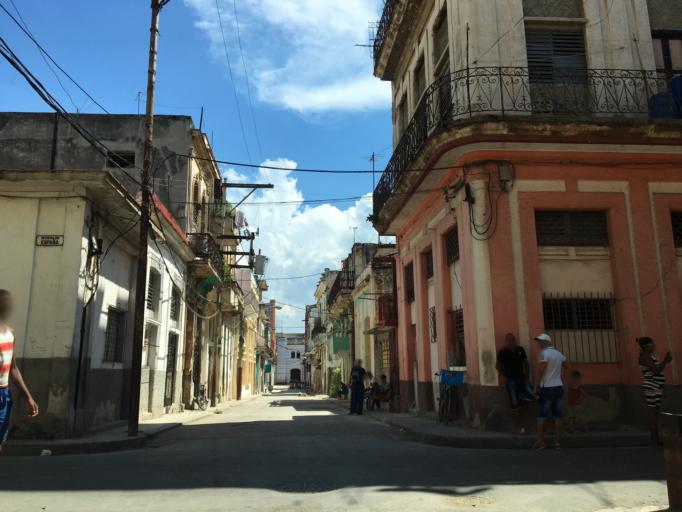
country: CU
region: La Habana
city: La Habana Vieja
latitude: 23.1279
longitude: -82.3581
